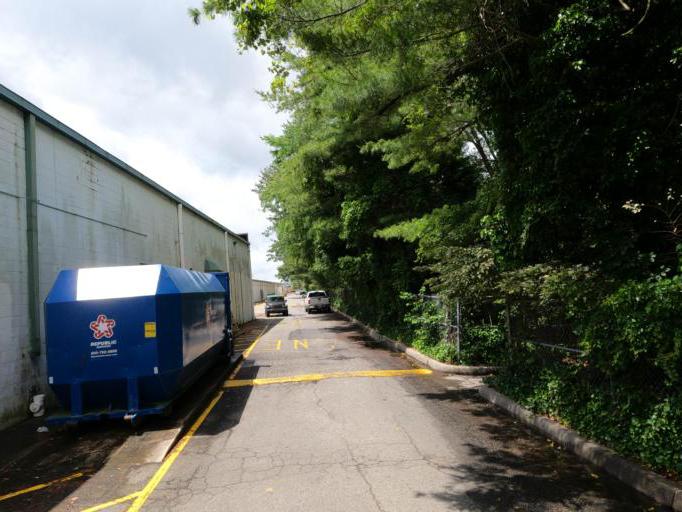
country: US
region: Delaware
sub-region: Sussex County
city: Lewes
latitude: 38.7294
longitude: -75.1327
